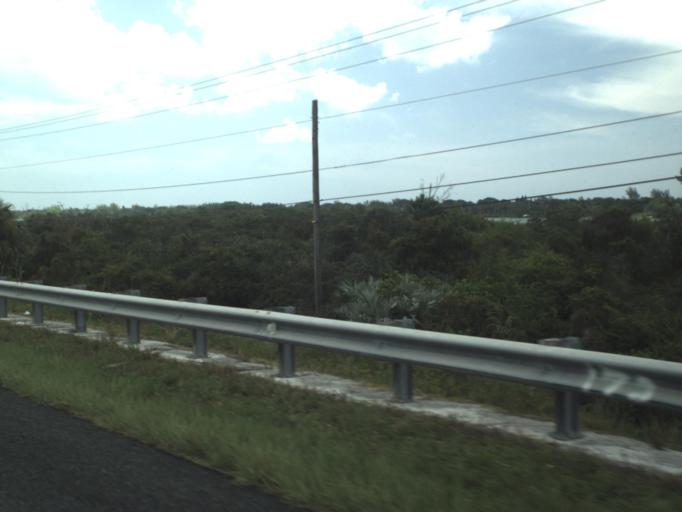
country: US
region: Florida
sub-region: Martin County
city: Hobe Sound
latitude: 27.0167
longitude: -80.1055
